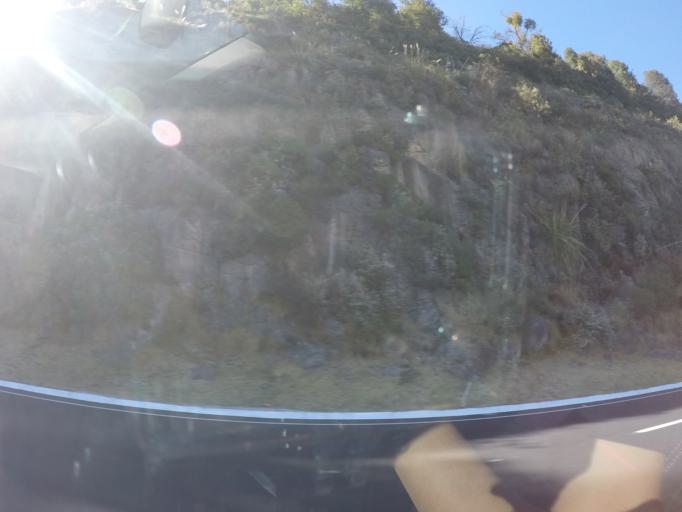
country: MX
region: Mexico City
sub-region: Cuajimalpa de Morelos
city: San Lorenzo Acopilco
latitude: 19.3161
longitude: -99.3383
